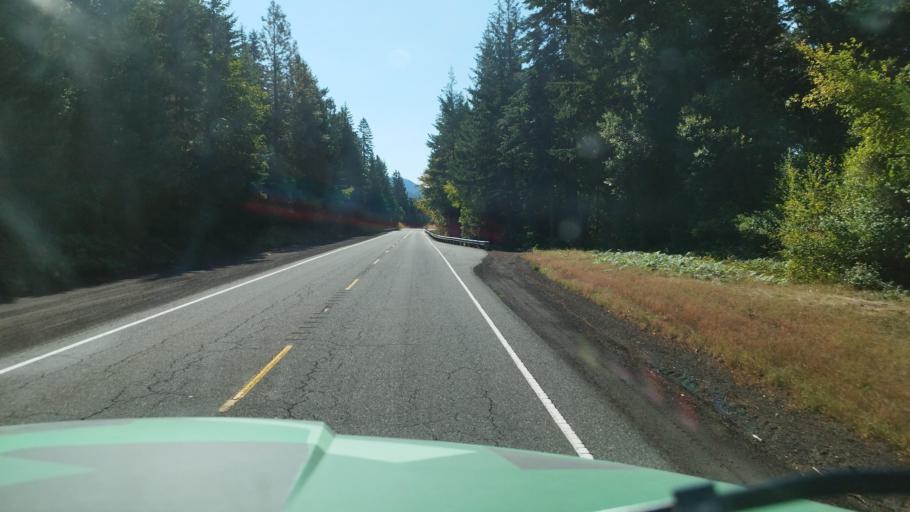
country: US
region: Oregon
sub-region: Hood River County
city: Odell
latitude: 45.5142
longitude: -121.5645
